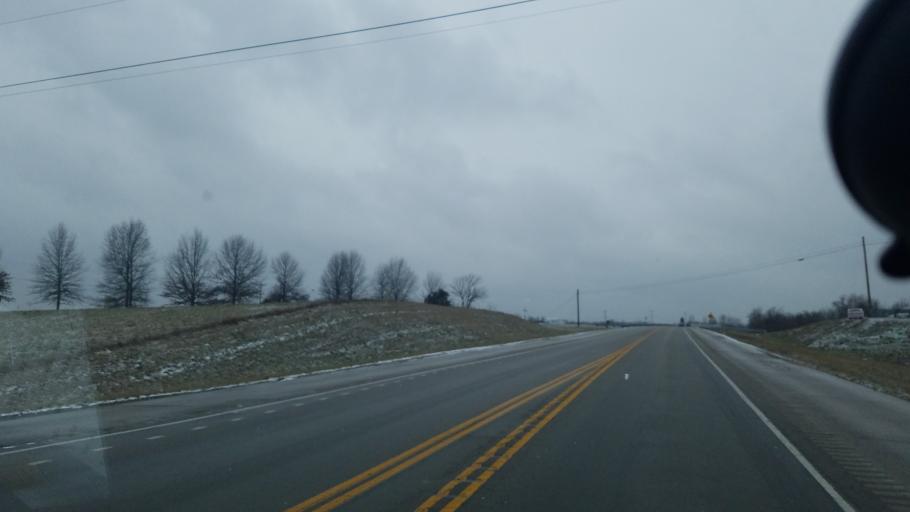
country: US
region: Kentucky
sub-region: Bath County
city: Owingsville
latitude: 38.2429
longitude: -83.8773
